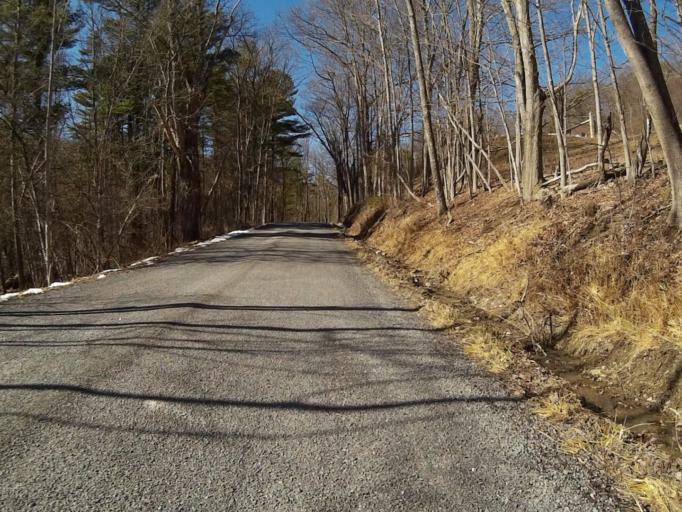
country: US
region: Pennsylvania
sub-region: Centre County
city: Stormstown
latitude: 40.8390
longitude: -78.0227
